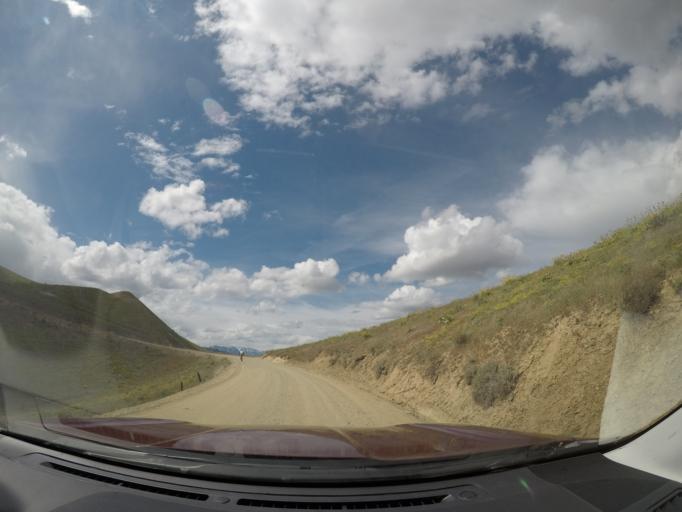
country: US
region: Washington
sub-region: Chelan County
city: West Wenatchee
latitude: 47.4635
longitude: -120.3691
